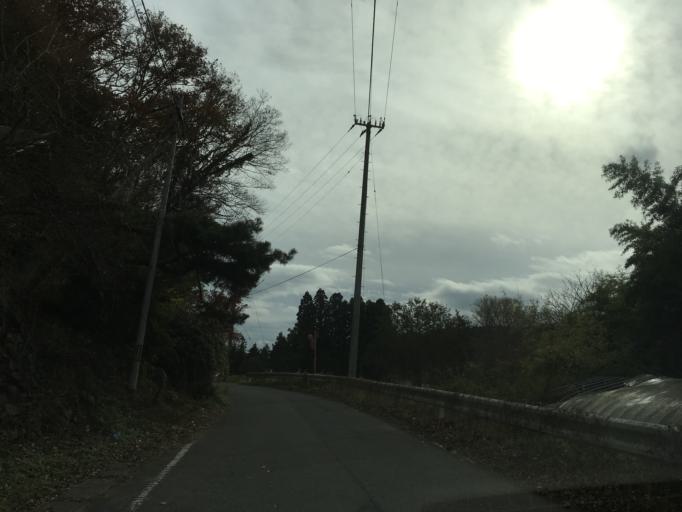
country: JP
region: Iwate
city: Ichinoseki
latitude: 38.7710
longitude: 141.2689
